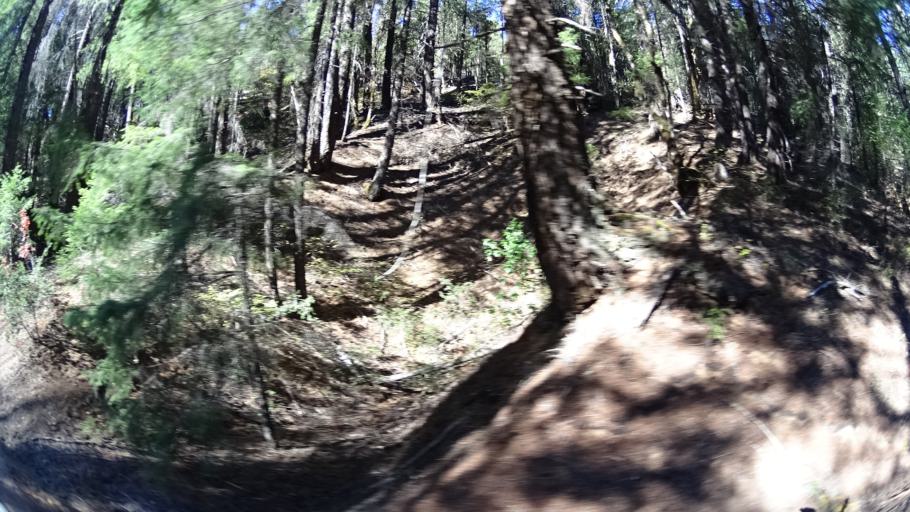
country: US
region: California
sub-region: Trinity County
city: Weaverville
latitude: 41.1942
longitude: -123.0732
